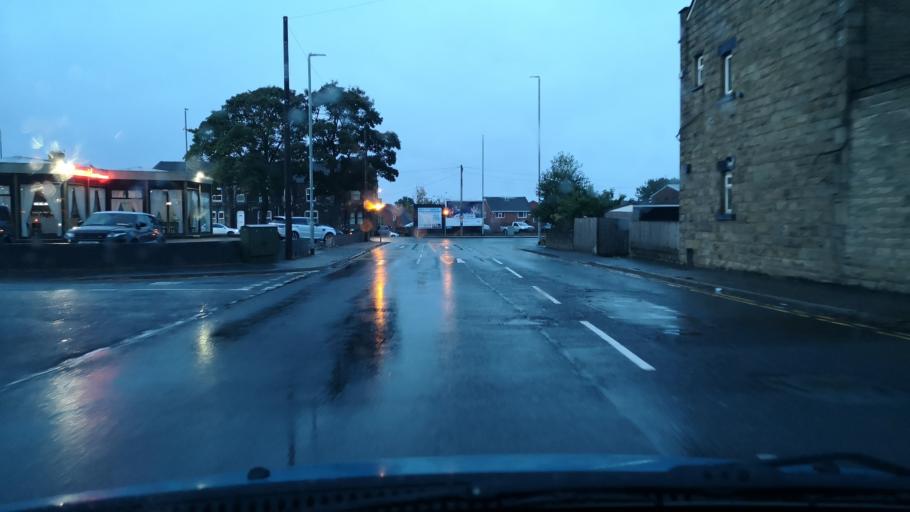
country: GB
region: England
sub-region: City and Borough of Leeds
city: Morley
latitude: 53.7362
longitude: -1.6084
